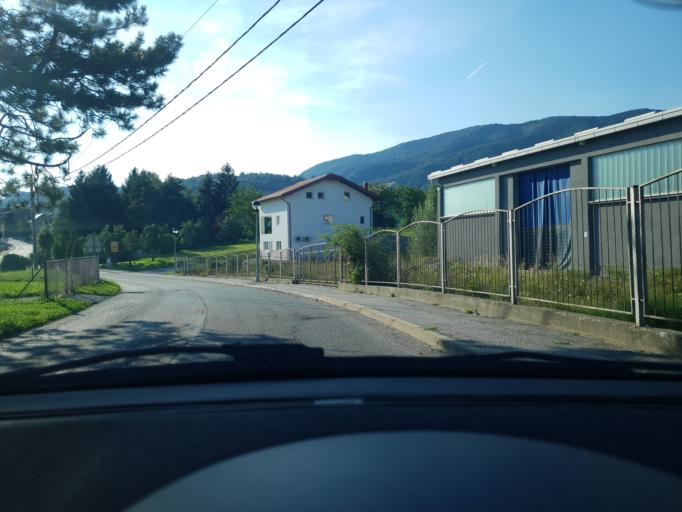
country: HR
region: Krapinsko-Zagorska
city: Radoboj
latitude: 46.1649
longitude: 15.9242
